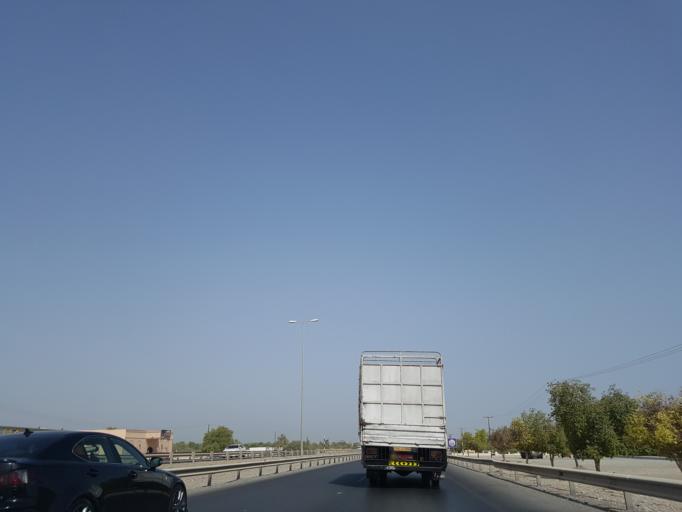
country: OM
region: Al Batinah
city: As Suwayq
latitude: 23.7564
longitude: 57.5616
